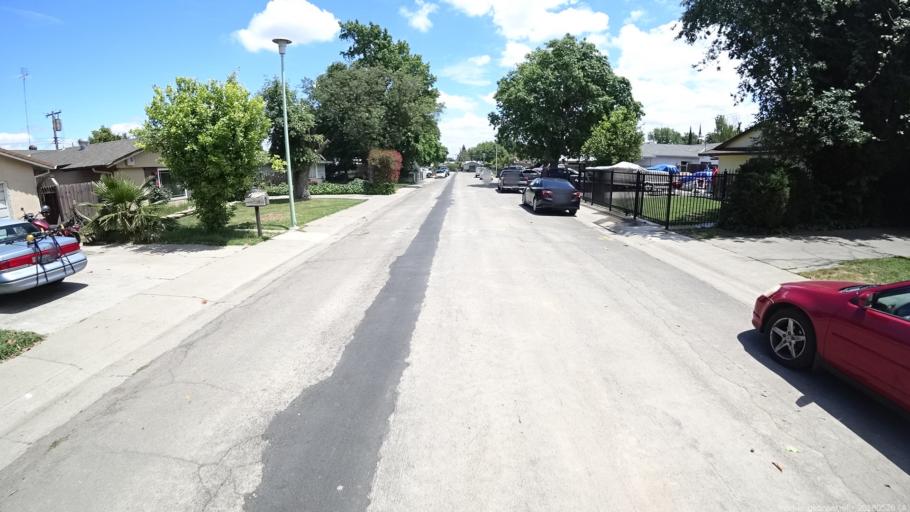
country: US
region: California
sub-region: Sacramento County
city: Sacramento
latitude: 38.6121
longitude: -121.4874
